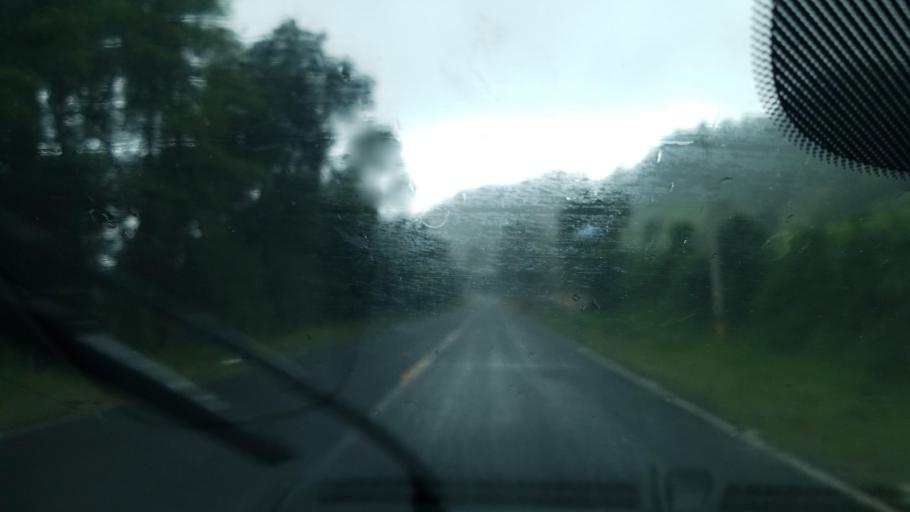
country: HN
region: Ocotepeque
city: La Labor
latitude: 14.4680
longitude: -89.0842
